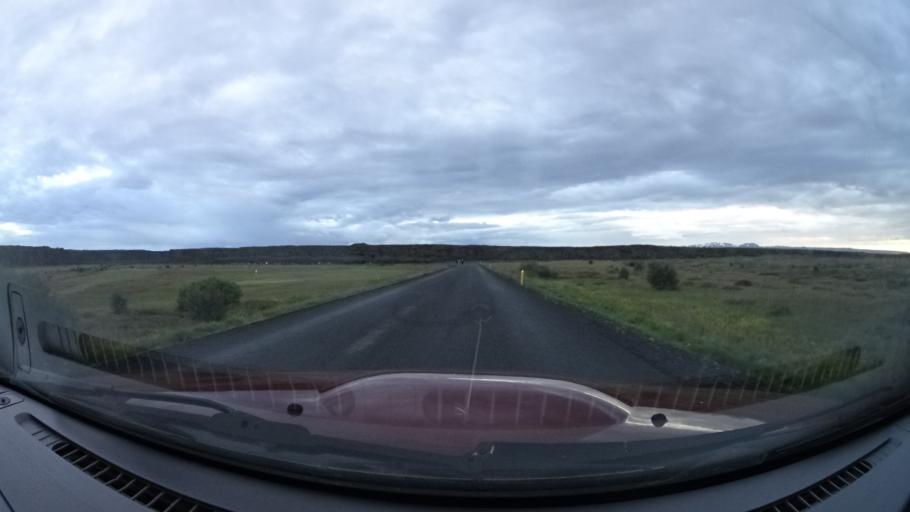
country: IS
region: Northeast
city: Husavik
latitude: 66.0286
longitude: -16.4897
